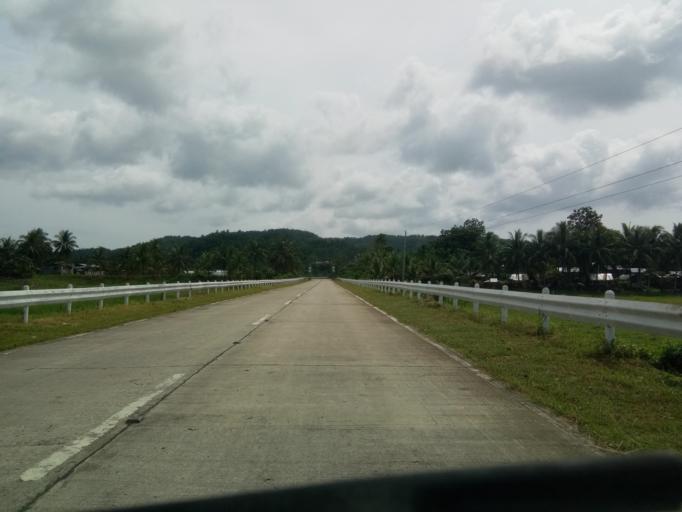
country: PH
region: Caraga
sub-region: Province of Surigao del Norte
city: Pilar
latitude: 9.8871
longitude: 126.0645
